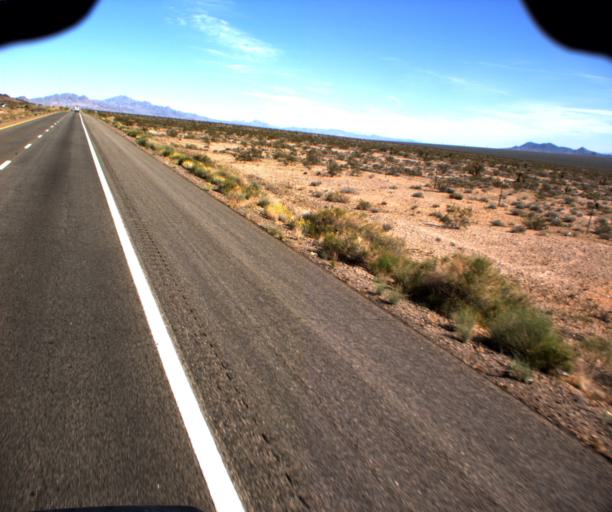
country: US
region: Arizona
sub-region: Mohave County
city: Dolan Springs
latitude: 35.7453
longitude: -114.4989
